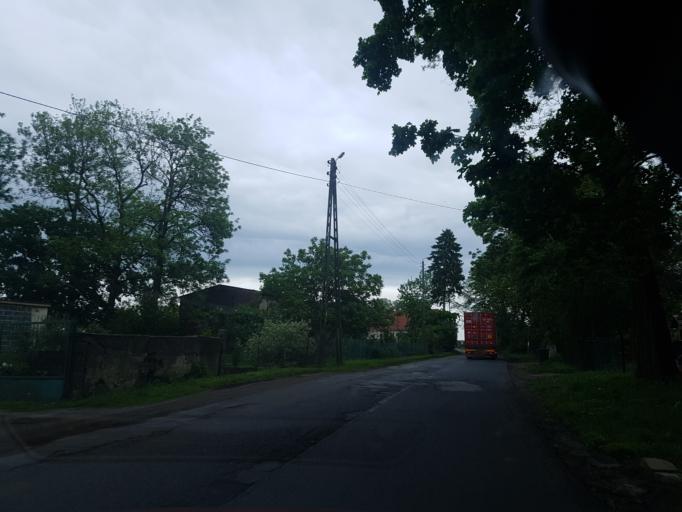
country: PL
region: Lower Silesian Voivodeship
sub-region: Powiat wroclawski
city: Zorawina
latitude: 50.9151
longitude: 16.9940
